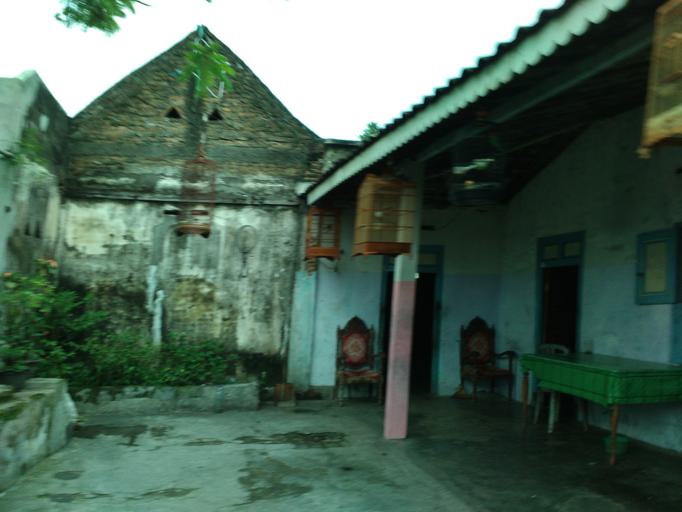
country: ID
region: Central Java
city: Gatak
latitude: -7.6047
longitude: 110.7023
